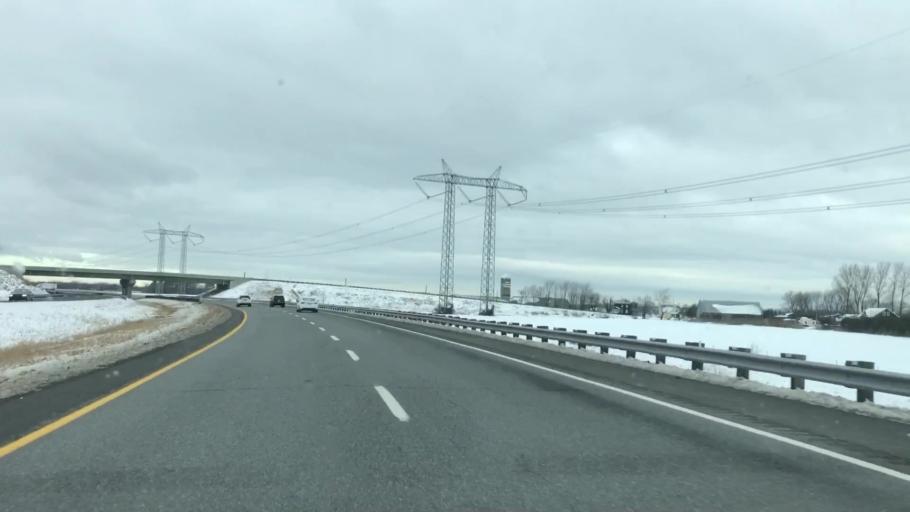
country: CA
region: Quebec
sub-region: Monteregie
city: Richelieu
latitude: 45.4167
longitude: -73.2158
